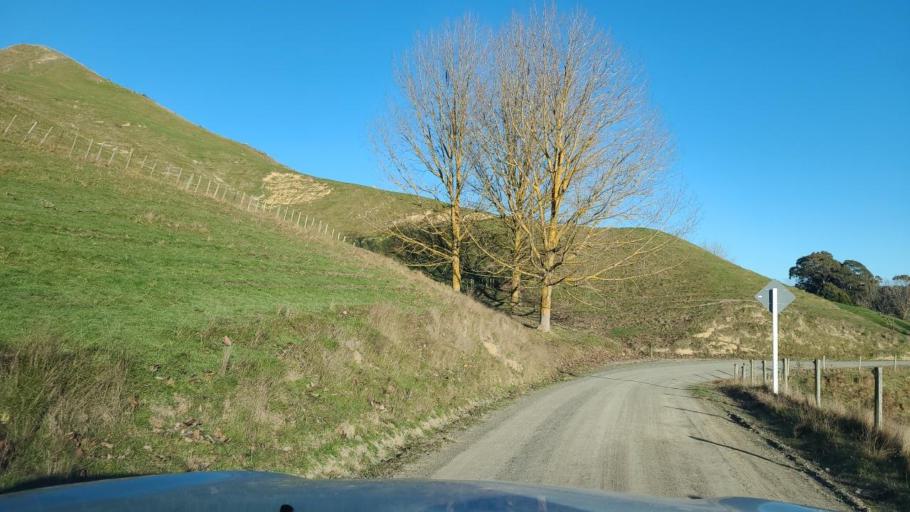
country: NZ
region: Hawke's Bay
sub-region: Hastings District
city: Hastings
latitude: -39.7968
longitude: 176.8265
